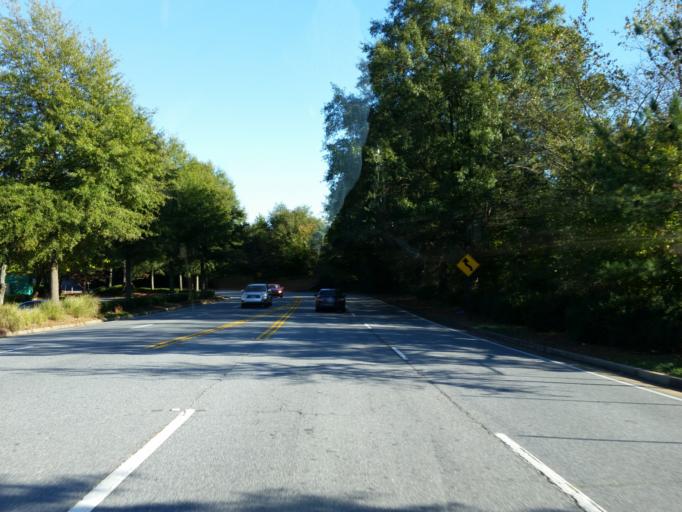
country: US
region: Georgia
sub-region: Cobb County
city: Vinings
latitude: 33.8943
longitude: -84.4630
